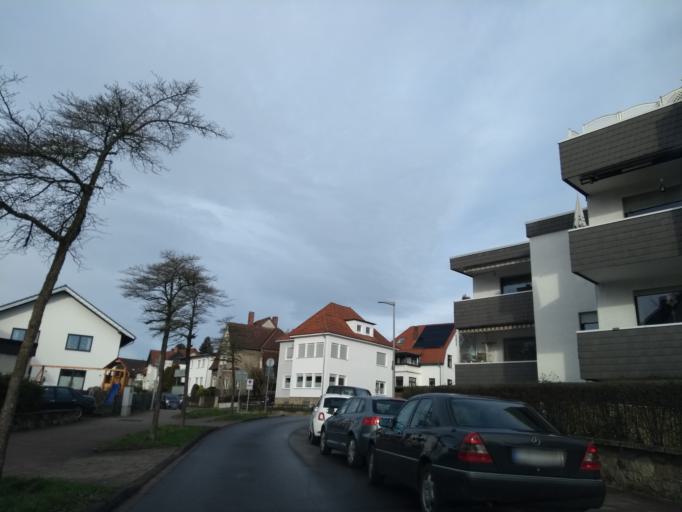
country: DE
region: North Rhine-Westphalia
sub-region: Regierungsbezirk Detmold
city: Lemgo
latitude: 52.0300
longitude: 8.8940
